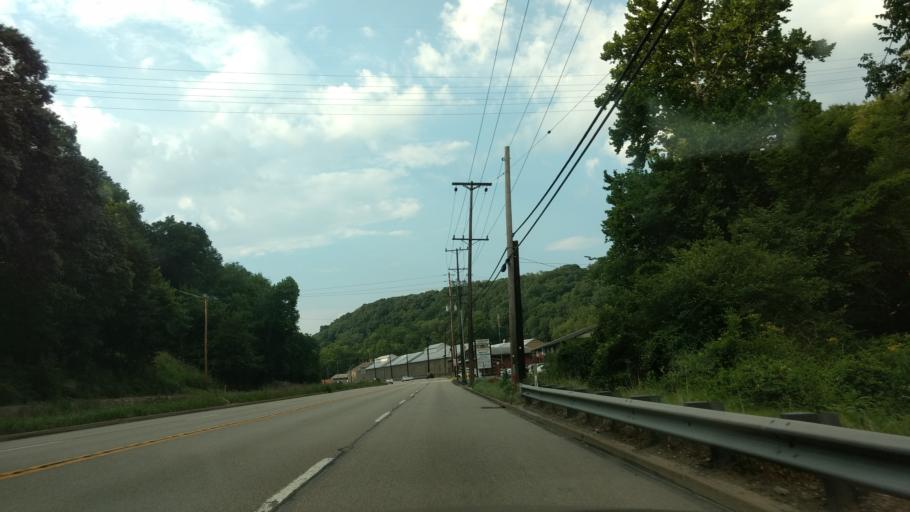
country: US
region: Pennsylvania
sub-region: Allegheny County
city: Allison Park
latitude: 40.5531
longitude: -79.9585
